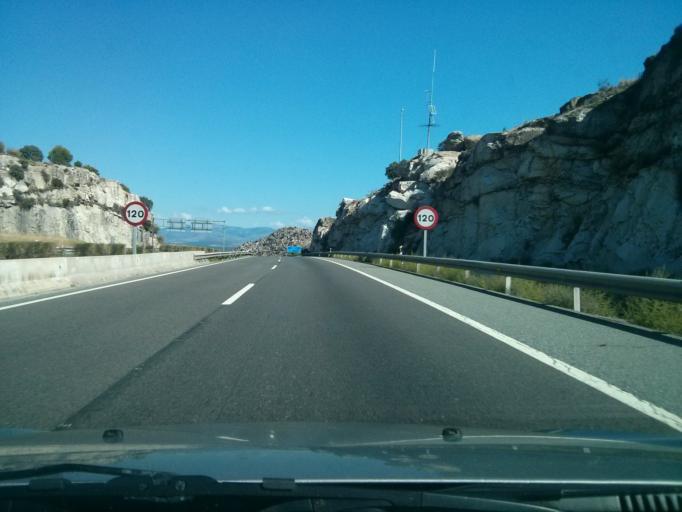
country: ES
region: Madrid
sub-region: Provincia de Madrid
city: La Cabrera
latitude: 40.8766
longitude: -3.6000
